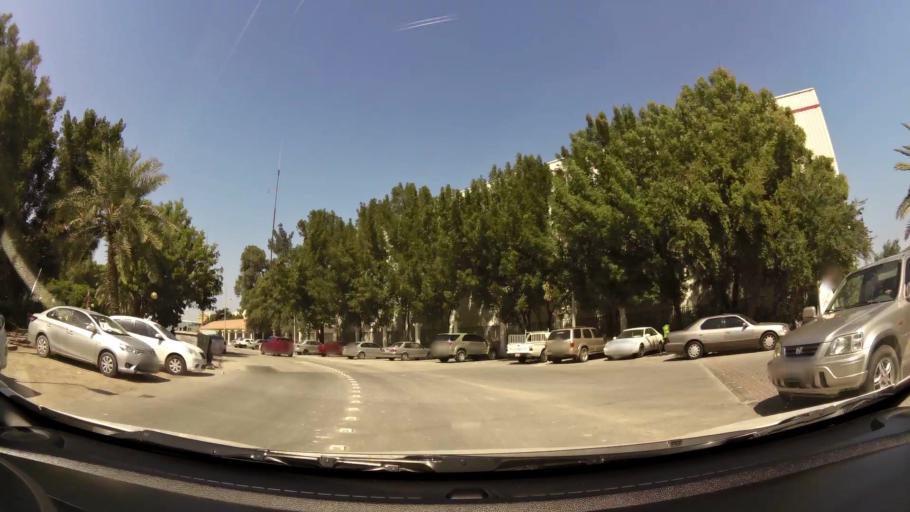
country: BH
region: Manama
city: Manama
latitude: 26.1976
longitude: 50.5985
